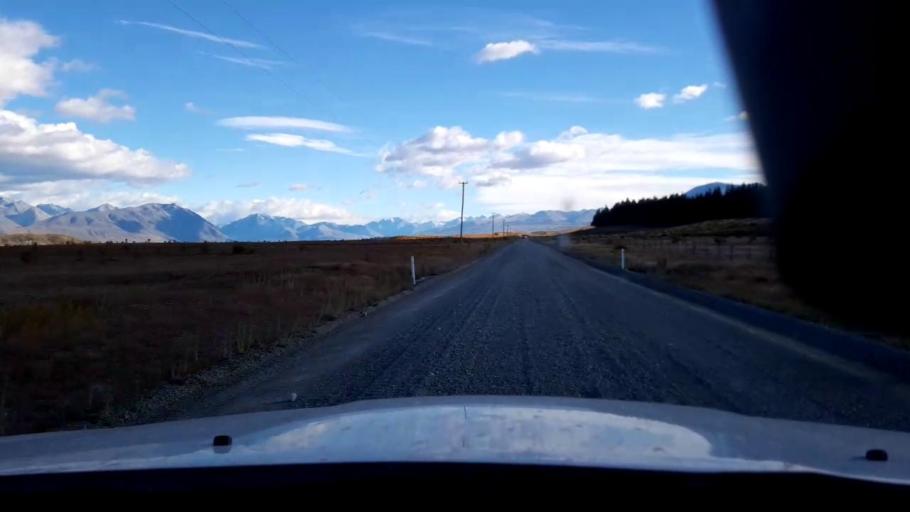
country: NZ
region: Canterbury
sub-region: Timaru District
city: Pleasant Point
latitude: -43.9869
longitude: 170.5050
